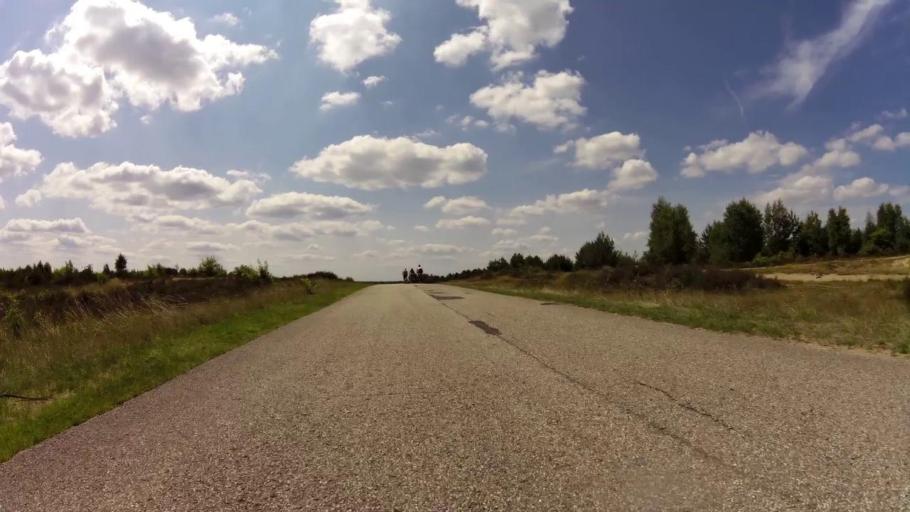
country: PL
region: West Pomeranian Voivodeship
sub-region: Powiat drawski
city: Drawsko Pomorskie
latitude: 53.4334
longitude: 15.7520
